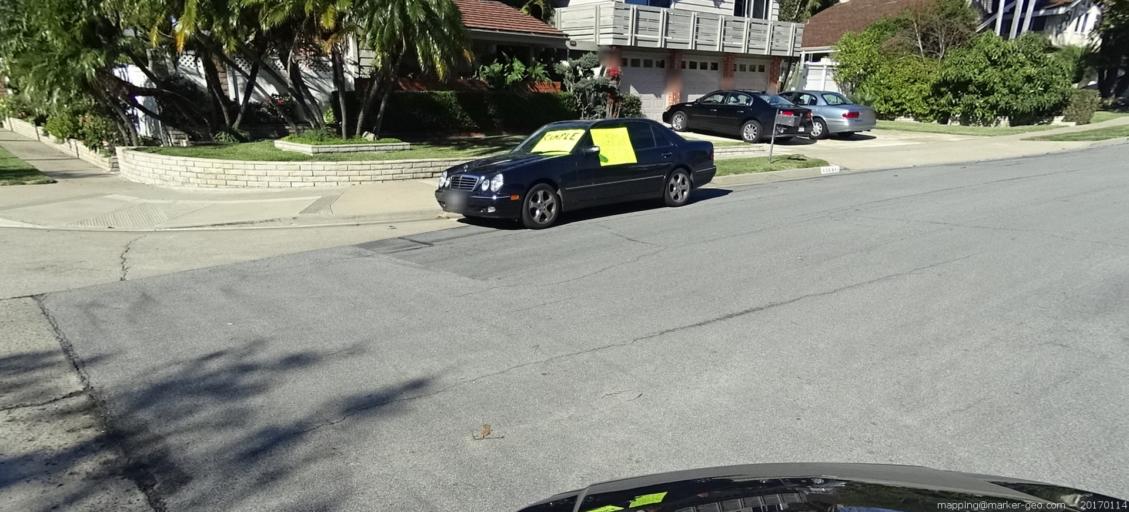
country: US
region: California
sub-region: Orange County
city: North Tustin
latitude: 33.7634
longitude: -117.8004
